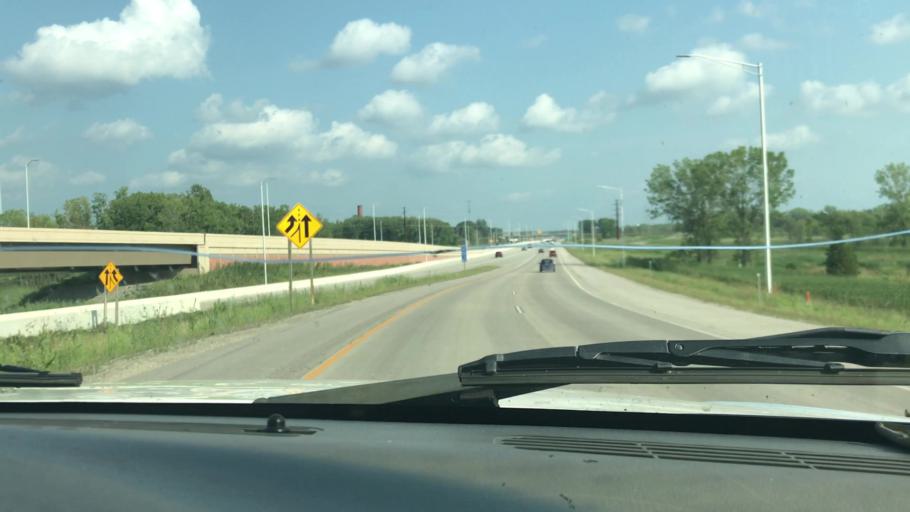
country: US
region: Wisconsin
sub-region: Brown County
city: Howard
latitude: 44.5581
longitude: -88.0504
